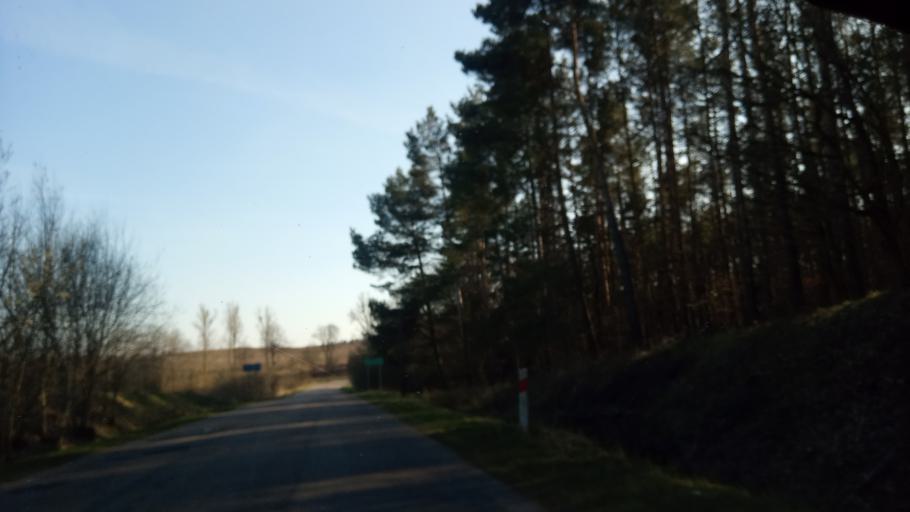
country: PL
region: West Pomeranian Voivodeship
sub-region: Powiat szczecinecki
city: Barwice
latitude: 53.6870
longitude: 16.3427
